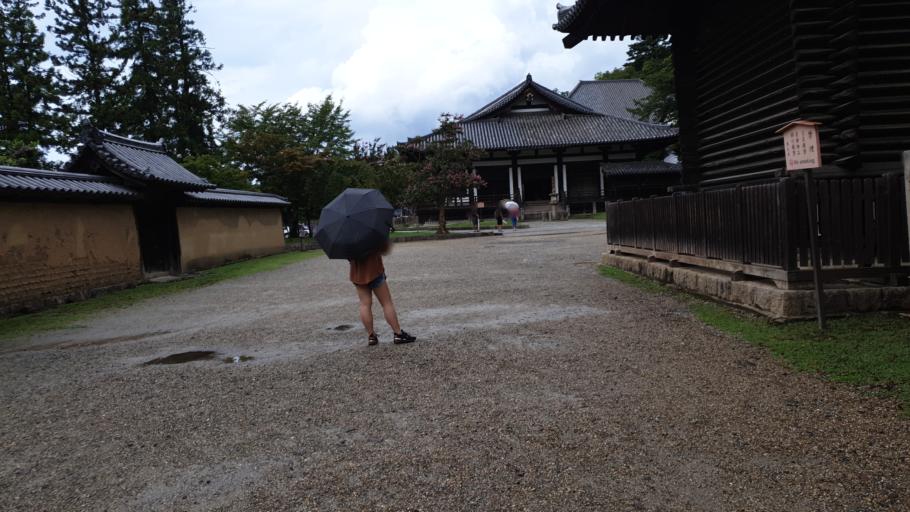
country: JP
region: Nara
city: Nara-shi
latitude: 34.6880
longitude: 135.8439
